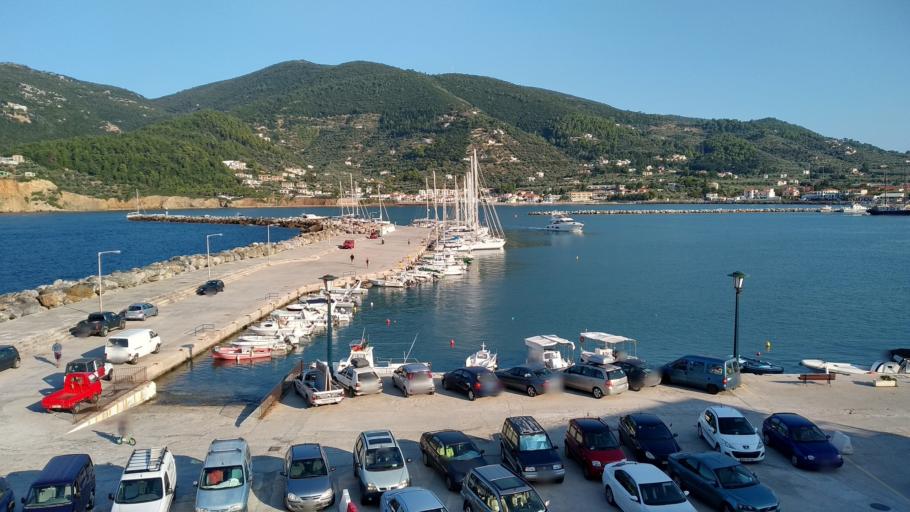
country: GR
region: Thessaly
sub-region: Nomos Magnisias
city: Skopelos
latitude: 39.1245
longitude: 23.7296
